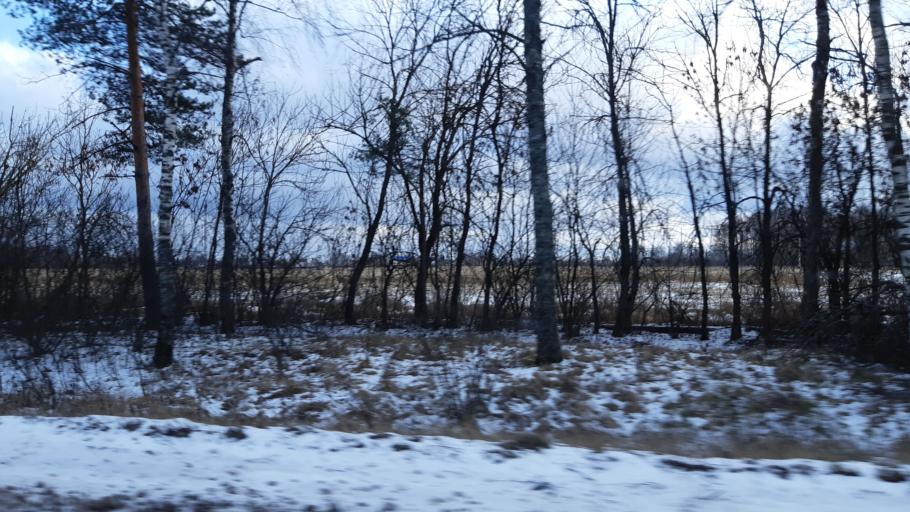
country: RU
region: Moskovskaya
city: Noginsk-9
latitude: 56.0015
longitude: 38.5497
